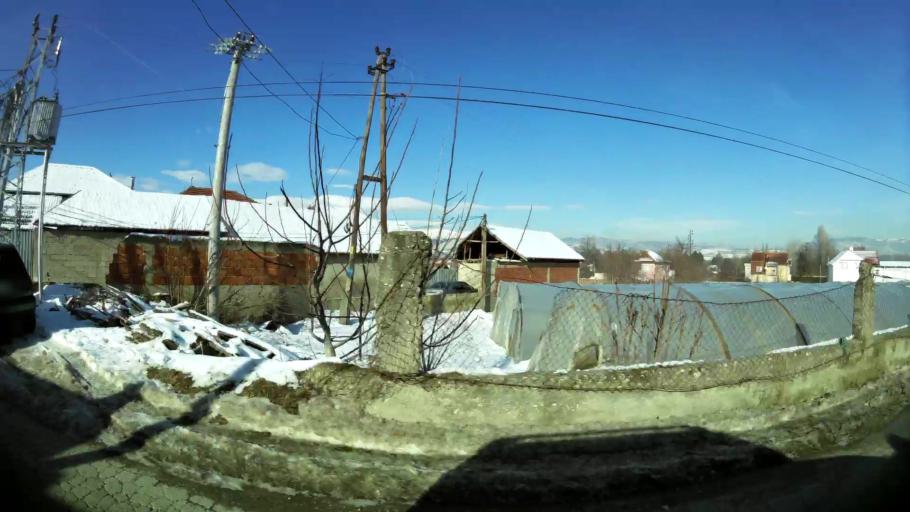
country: MK
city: Grchec
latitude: 41.9956
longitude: 21.3424
